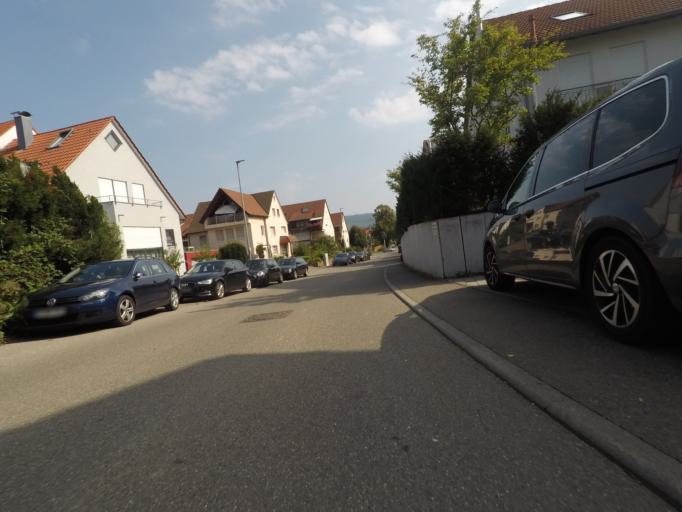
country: DE
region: Baden-Wuerttemberg
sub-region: Regierungsbezirk Stuttgart
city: Weinstadt-Endersbach
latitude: 48.8041
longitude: 9.3819
